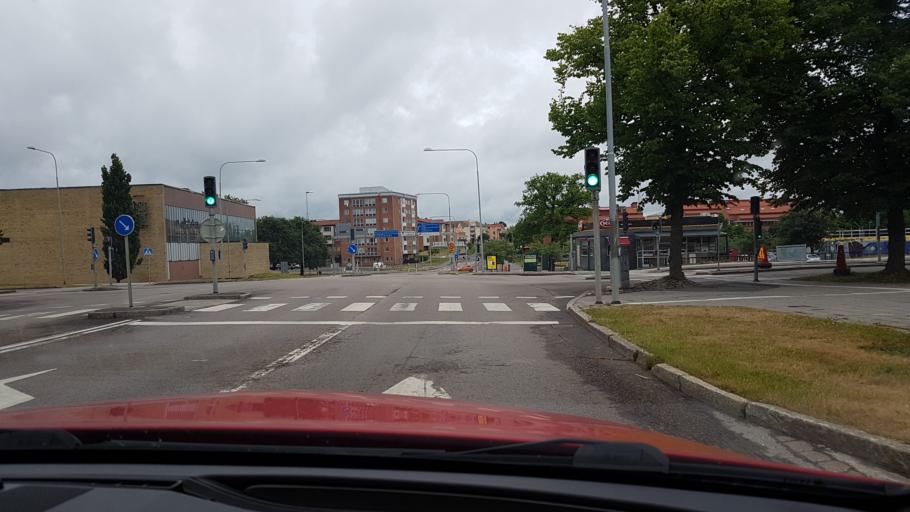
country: SE
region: Vaestra Goetaland
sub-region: Skovde Kommun
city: Skoevde
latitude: 58.3910
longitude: 13.8522
